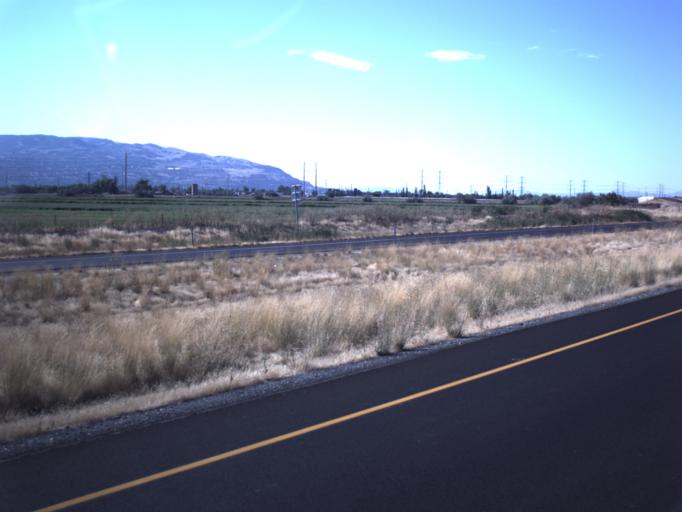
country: US
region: Utah
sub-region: Davis County
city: West Bountiful
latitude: 40.8931
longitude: -111.9344
